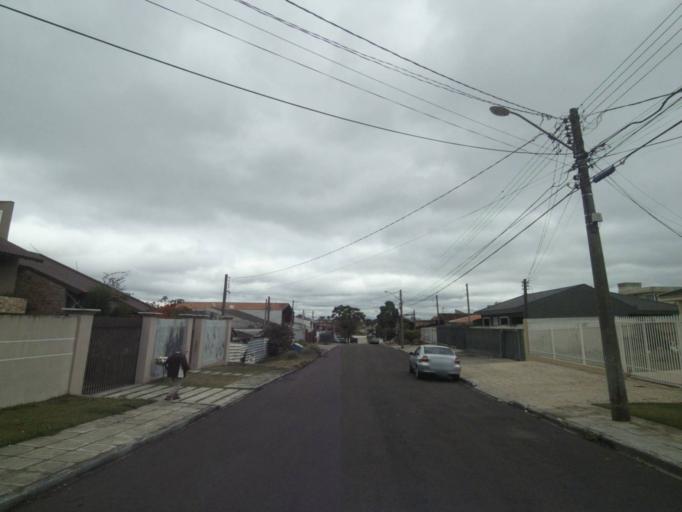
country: BR
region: Parana
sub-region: Curitiba
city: Curitiba
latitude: -25.4982
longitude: -49.2875
